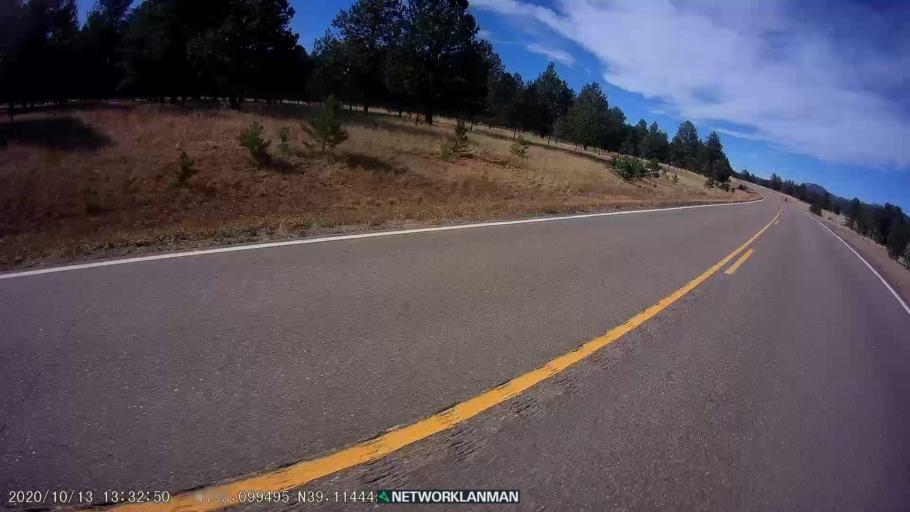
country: US
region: Colorado
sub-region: Teller County
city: Woodland Park
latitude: 39.1145
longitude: -105.0994
